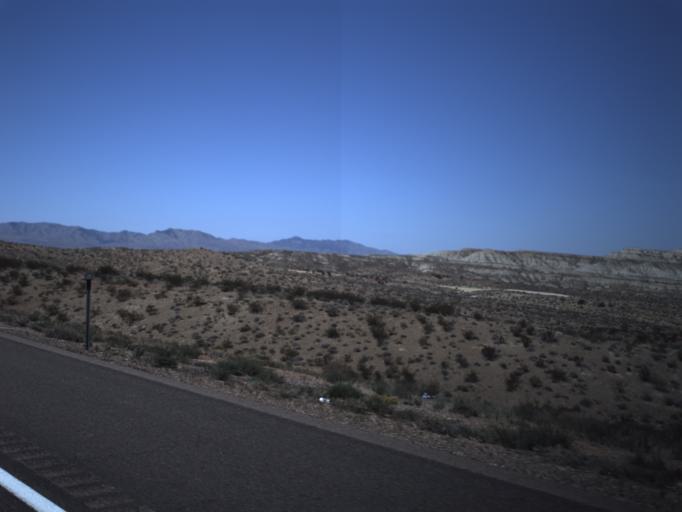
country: US
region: Utah
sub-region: Washington County
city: Saint George
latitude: 37.0053
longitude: -113.5384
